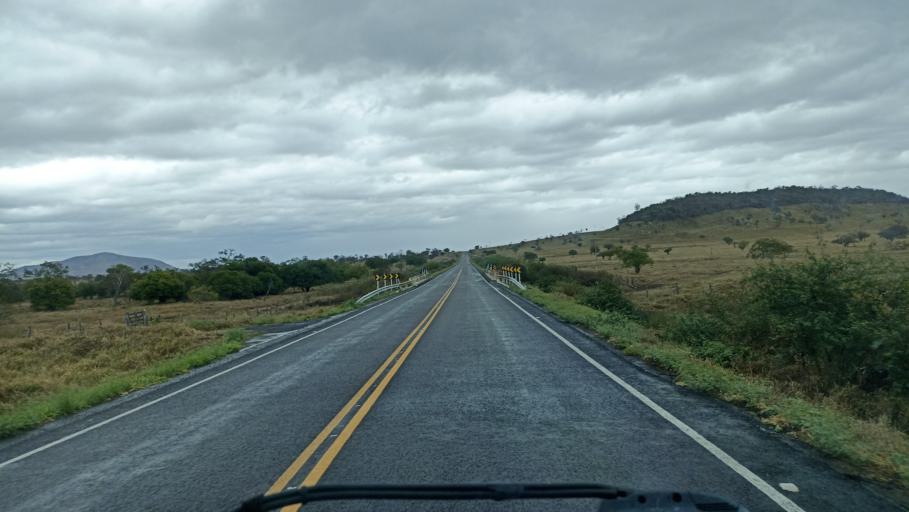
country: BR
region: Bahia
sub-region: Iacu
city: Iacu
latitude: -12.9627
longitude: -40.4825
